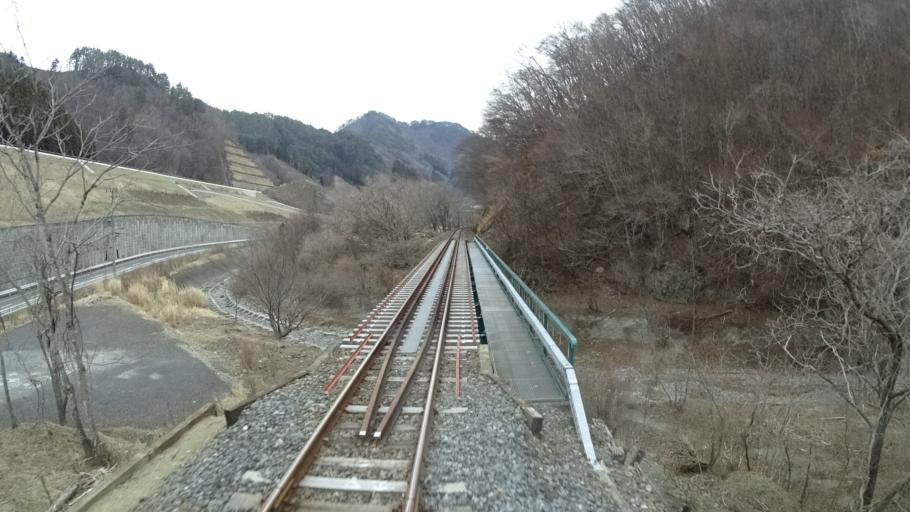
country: JP
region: Iwate
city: Kamaishi
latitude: 39.2970
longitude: 141.8684
